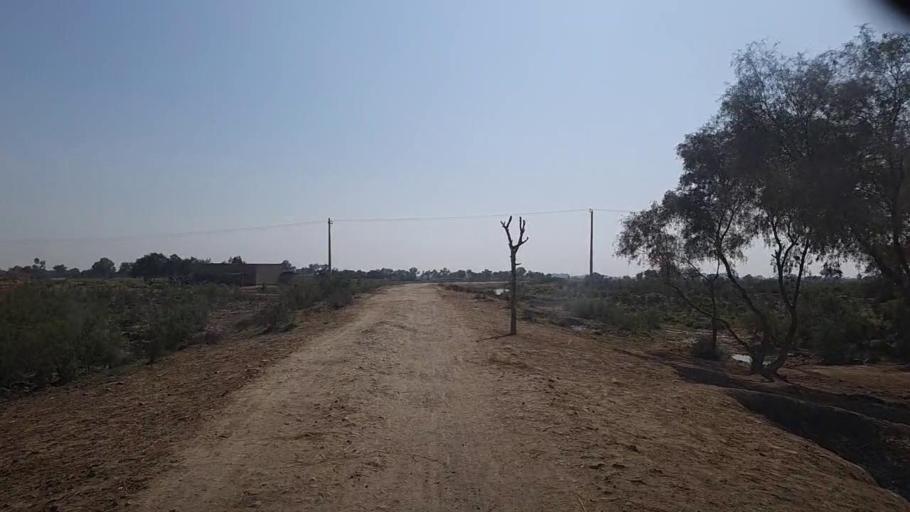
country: PK
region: Sindh
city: Thul
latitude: 28.1699
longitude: 68.7668
